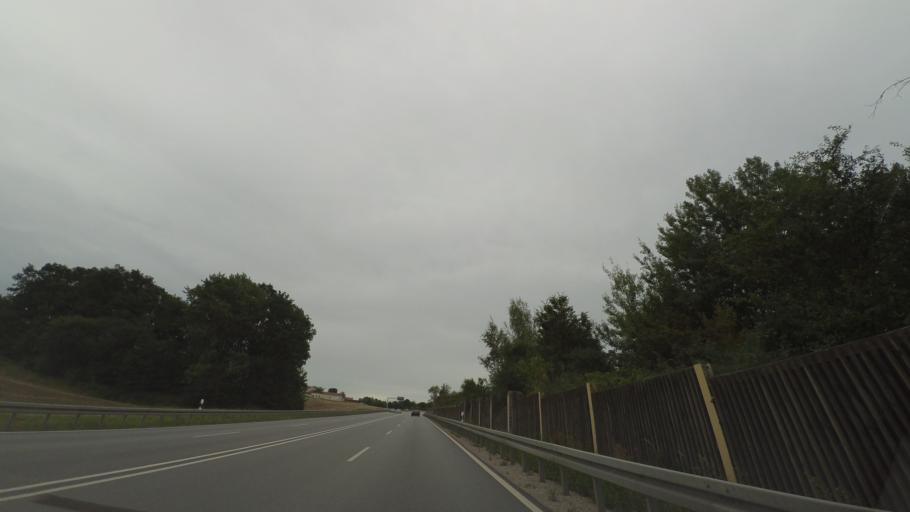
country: DE
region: Bavaria
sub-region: Upper Palatinate
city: Breitenbrunn
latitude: 49.3738
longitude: 12.0281
